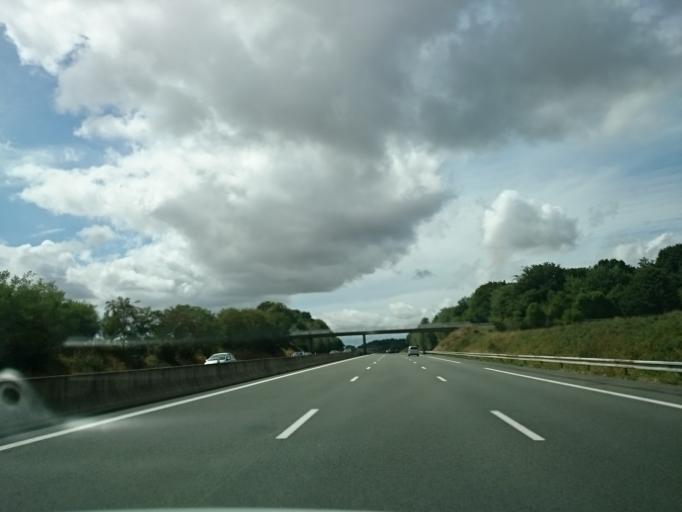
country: FR
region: Centre
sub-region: Departement d'Eure-et-Loir
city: Brou
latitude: 48.2701
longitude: 1.1590
